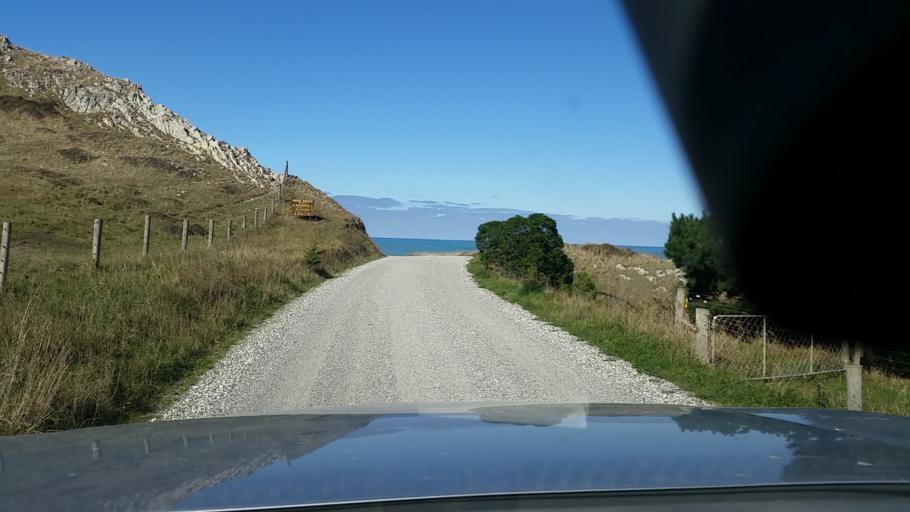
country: NZ
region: Marlborough
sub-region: Marlborough District
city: Blenheim
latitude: -41.8434
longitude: 174.1817
